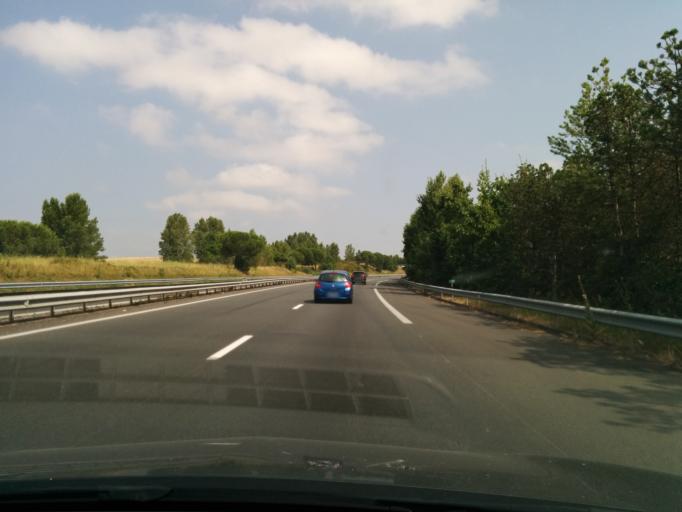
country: FR
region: Midi-Pyrenees
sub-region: Departement de la Haute-Garonne
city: Garidech
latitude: 43.7120
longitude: 1.5663
